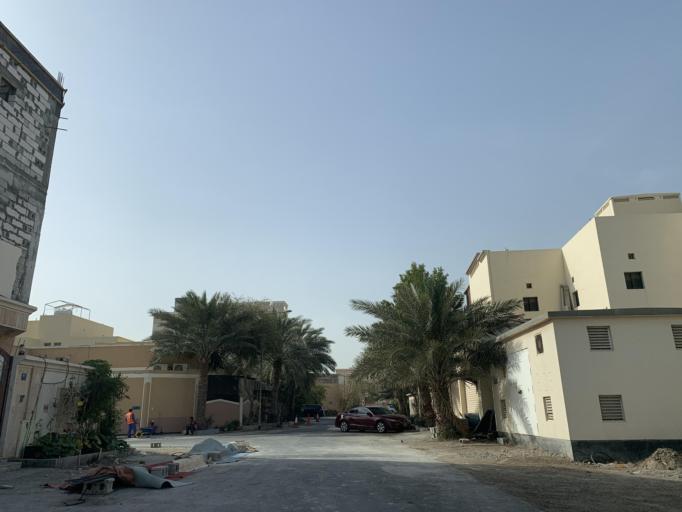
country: BH
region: Northern
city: Madinat `Isa
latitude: 26.1828
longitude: 50.5637
